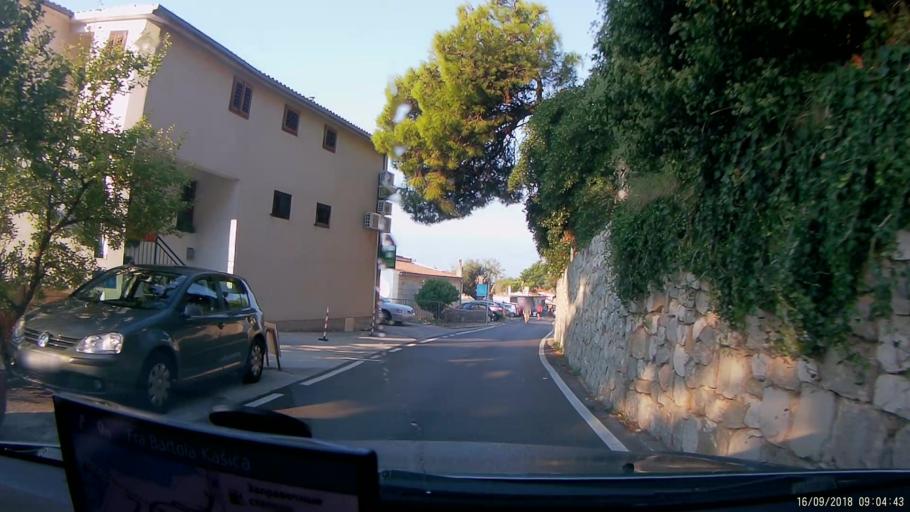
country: HR
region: Splitsko-Dalmatinska
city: Donja Brela
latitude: 43.3685
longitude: 16.9323
